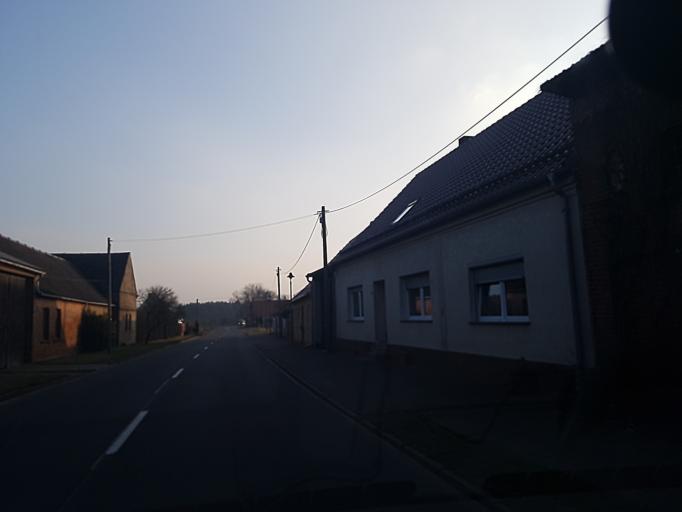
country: DE
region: Saxony-Anhalt
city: Coswig
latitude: 51.9950
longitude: 12.4720
